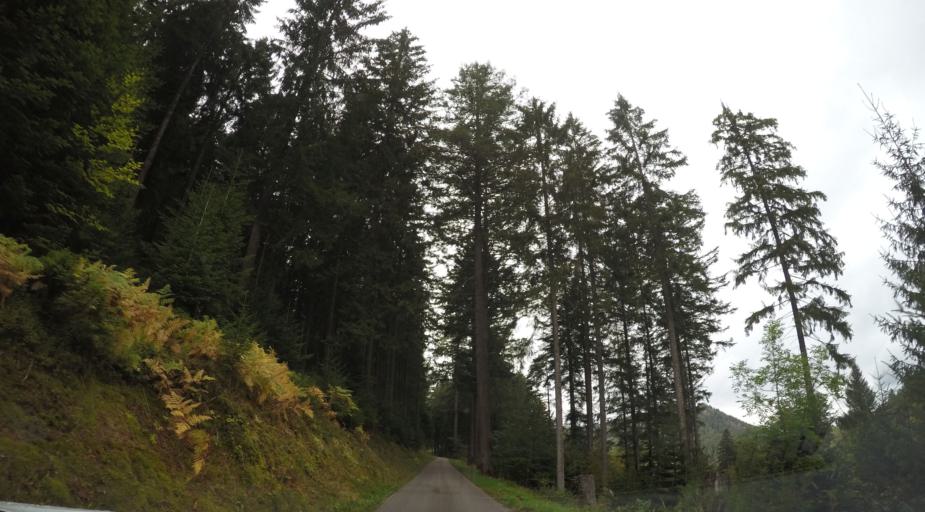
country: DE
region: Baden-Wuerttemberg
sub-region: Karlsruhe Region
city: Baiersbronn
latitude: 48.4940
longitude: 8.3223
